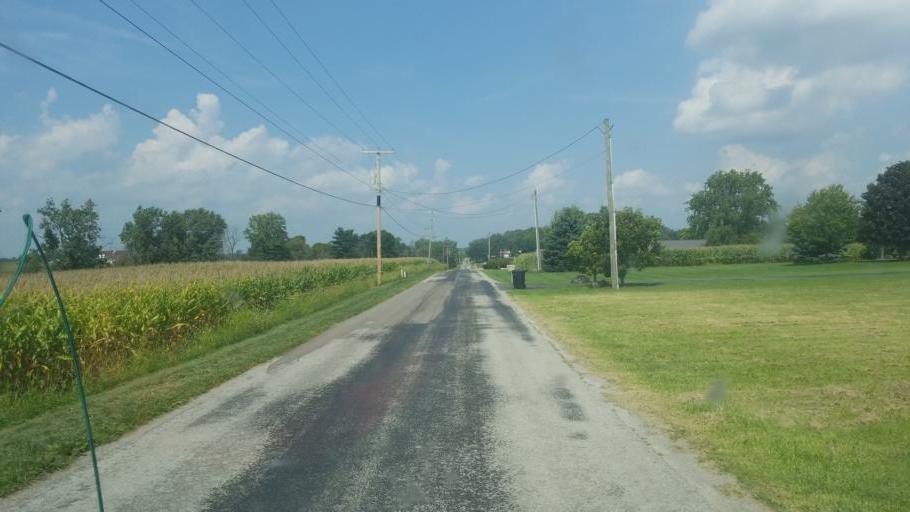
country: US
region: Ohio
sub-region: Richland County
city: Shelby
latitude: 40.8803
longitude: -82.5956
